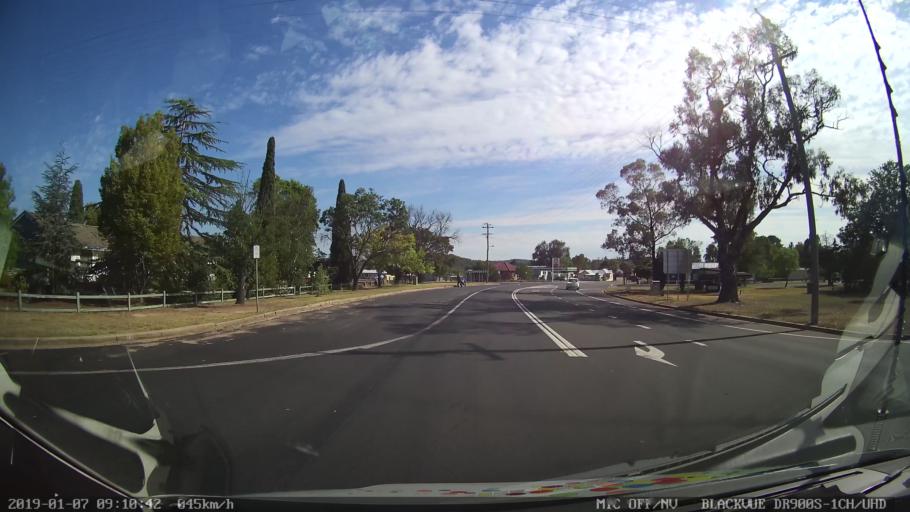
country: AU
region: New South Wales
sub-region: Armidale Dumaresq
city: Armidale
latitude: -30.6467
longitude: 151.4928
